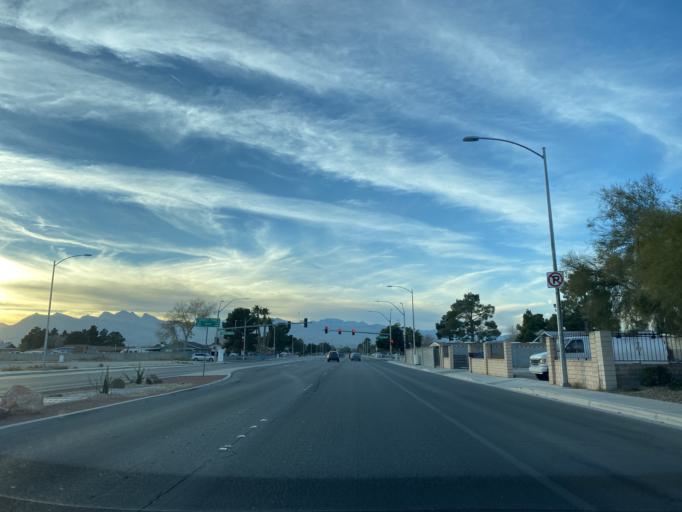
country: US
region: Nevada
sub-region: Clark County
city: Las Vegas
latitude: 36.2620
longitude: -115.2328
